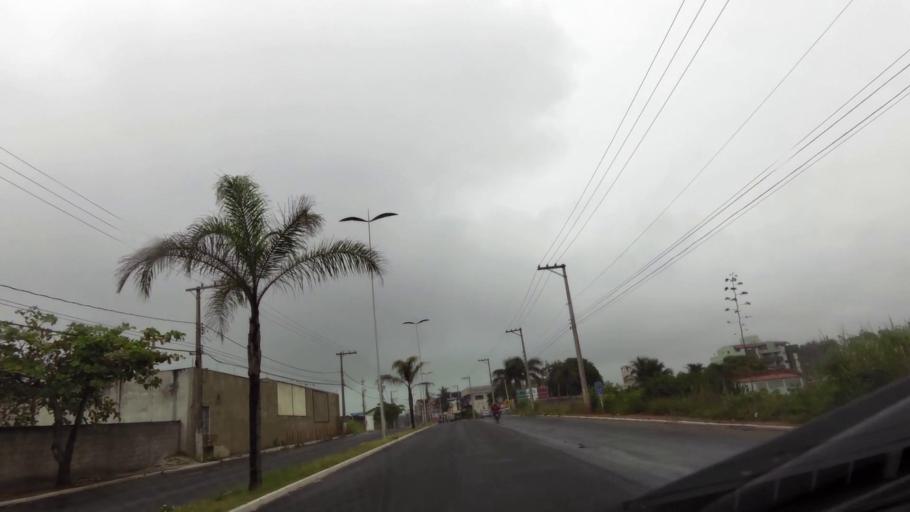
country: BR
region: Espirito Santo
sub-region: Guarapari
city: Guarapari
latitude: -20.7269
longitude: -40.5289
